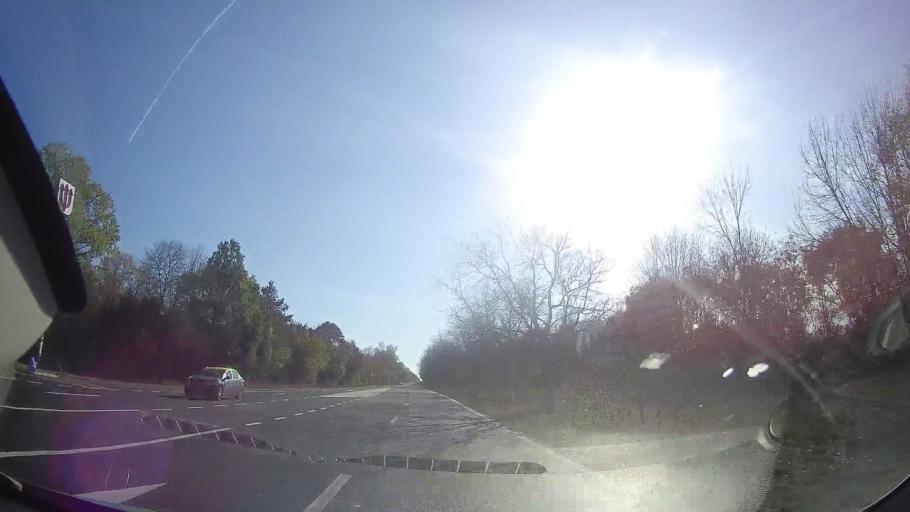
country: RO
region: Constanta
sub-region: Comuna Douazeci si Trei August
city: Dulcesti
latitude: 43.8752
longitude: 28.5740
